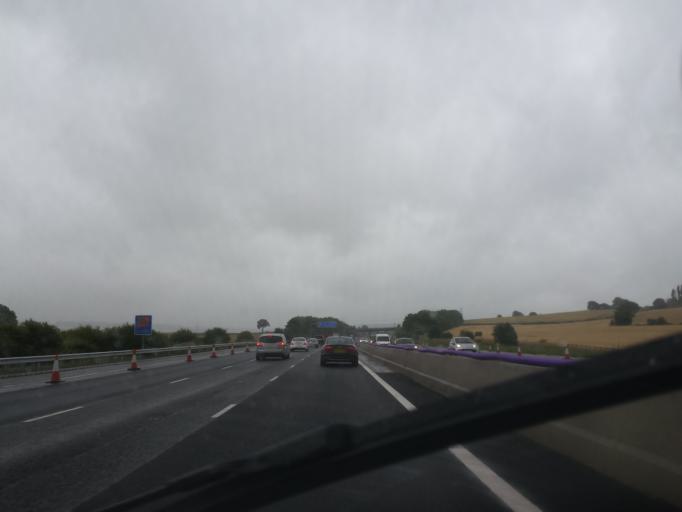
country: GB
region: England
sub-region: Derbyshire
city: Bolsover
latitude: 53.2207
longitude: -1.3283
